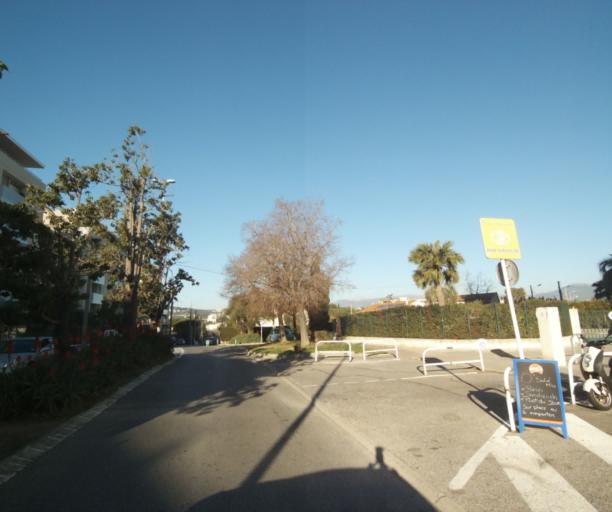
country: FR
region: Provence-Alpes-Cote d'Azur
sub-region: Departement des Alpes-Maritimes
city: Antibes
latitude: 43.5834
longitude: 7.1082
